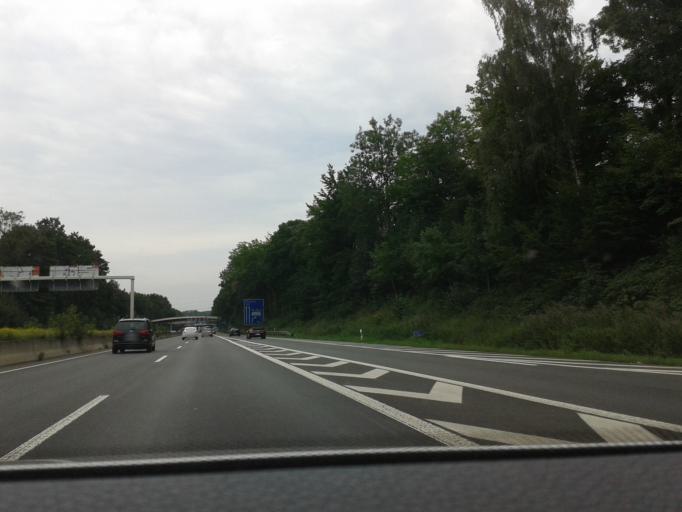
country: DE
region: North Rhine-Westphalia
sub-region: Regierungsbezirk Arnsberg
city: Bochum
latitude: 51.4969
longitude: 7.2785
